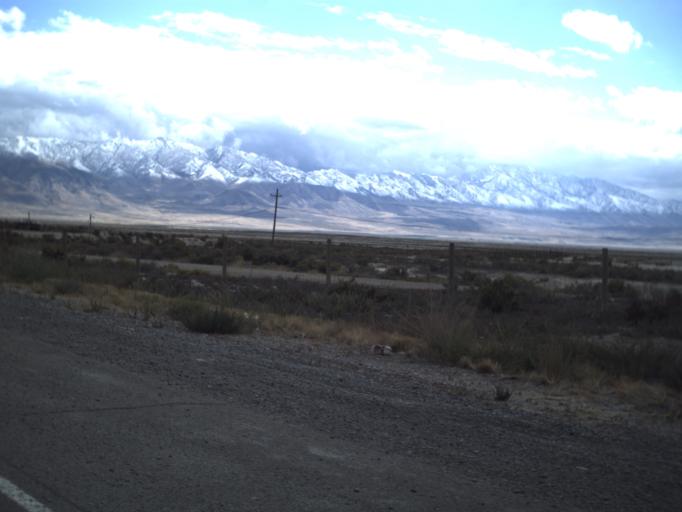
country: US
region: Utah
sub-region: Tooele County
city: Grantsville
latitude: 40.7618
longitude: -112.7809
